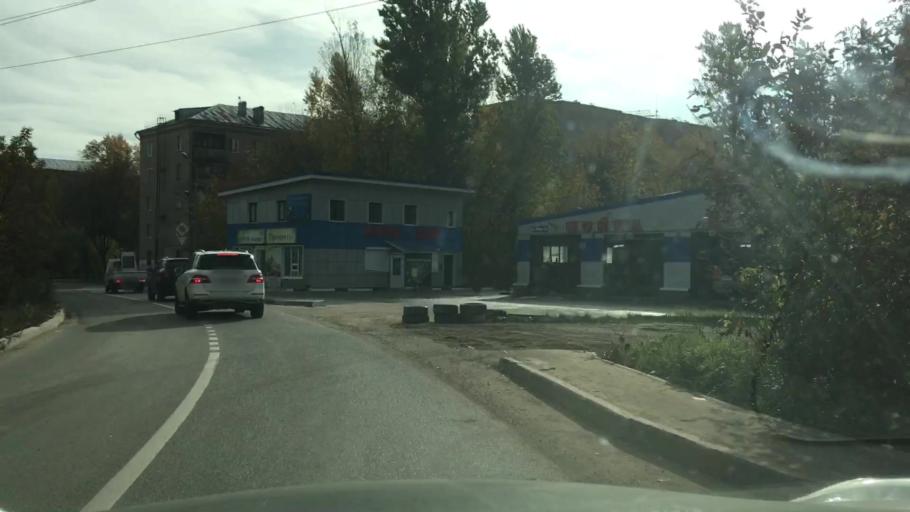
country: RU
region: Moskovskaya
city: Balashikha
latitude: 55.8043
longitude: 37.9261
